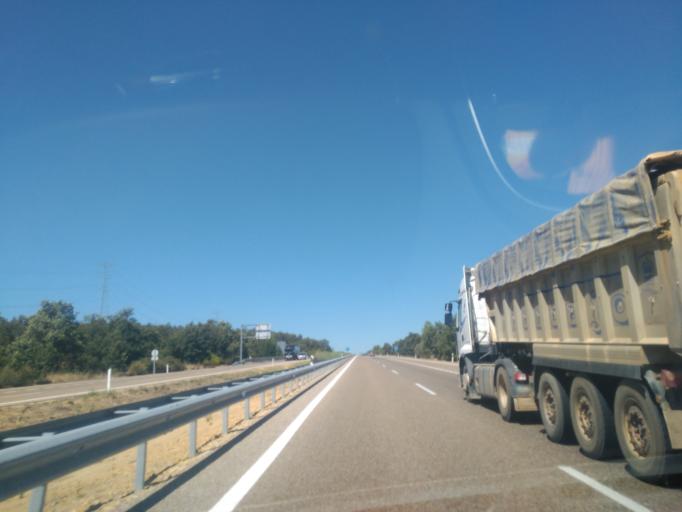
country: ES
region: Castille and Leon
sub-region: Provincia de Zamora
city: Mombuey
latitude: 42.0192
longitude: -6.3479
